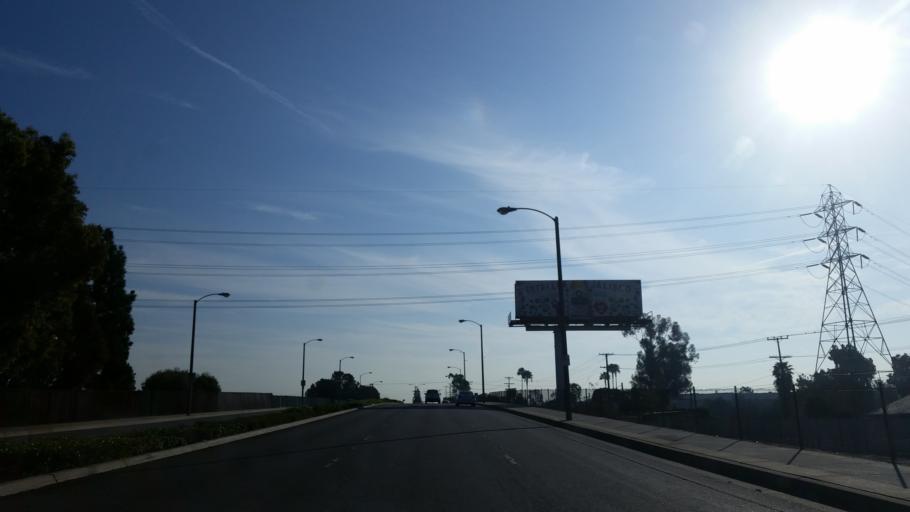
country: US
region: California
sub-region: Los Angeles County
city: Bellflower
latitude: 33.8879
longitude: -118.1109
